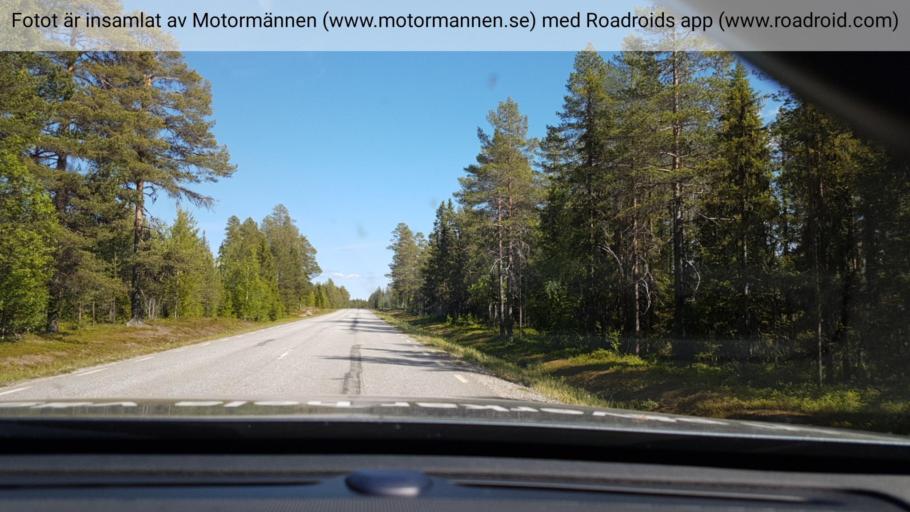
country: SE
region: Vaesterbotten
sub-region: Lycksele Kommun
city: Soderfors
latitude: 64.6246
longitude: 18.0903
